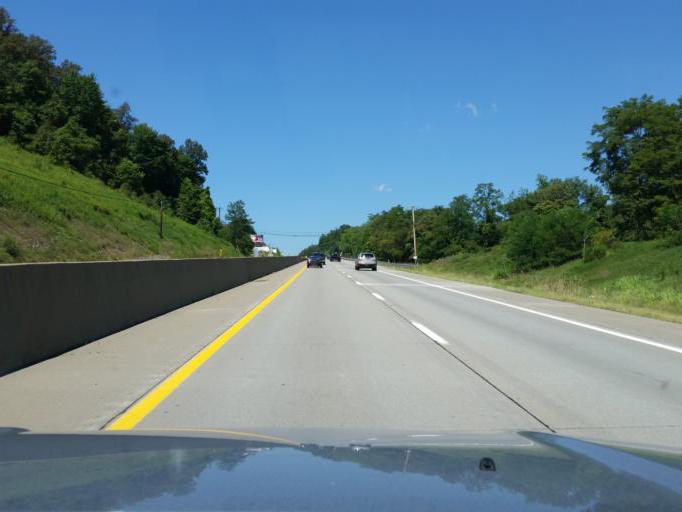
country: US
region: Pennsylvania
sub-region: Westmoreland County
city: Delmont
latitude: 40.4000
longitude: -79.5086
